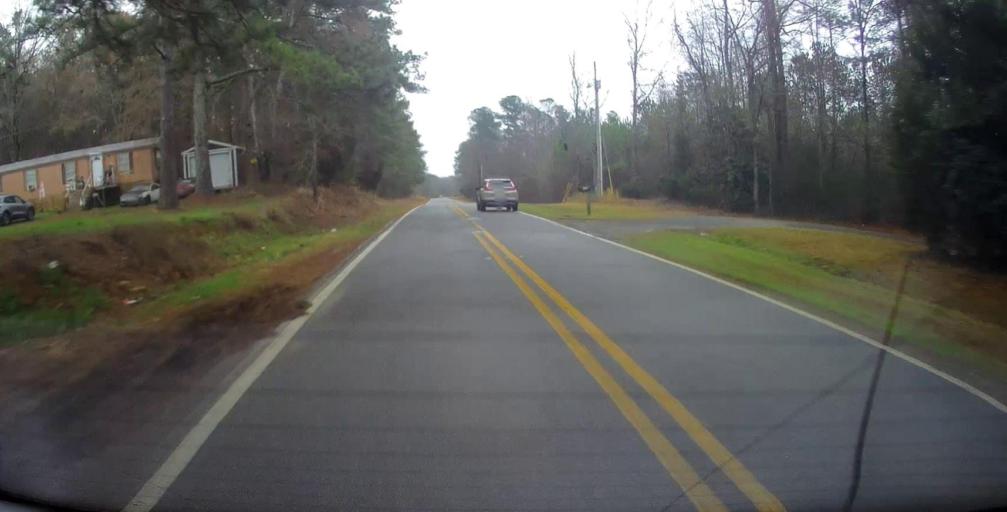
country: US
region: Georgia
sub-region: Monroe County
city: Forsyth
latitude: 33.1176
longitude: -83.9634
